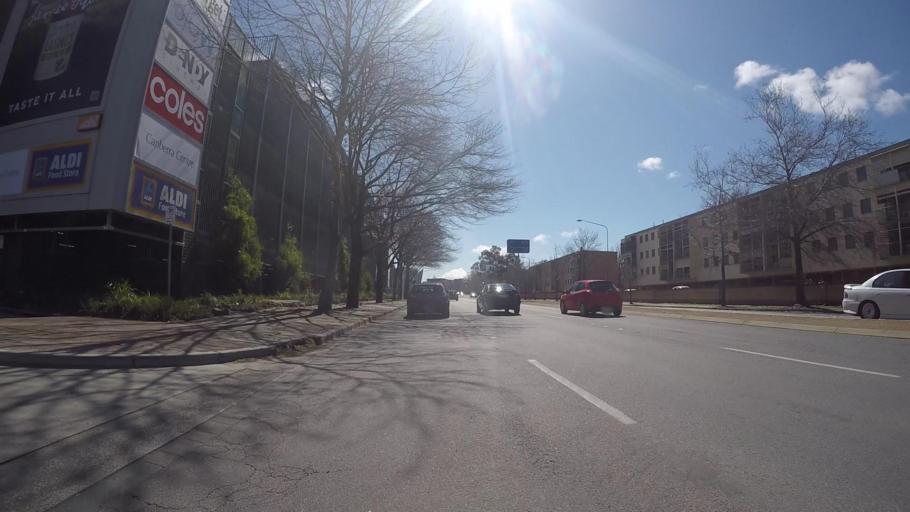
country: AU
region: Australian Capital Territory
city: Canberra
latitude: -35.2791
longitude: 149.1353
